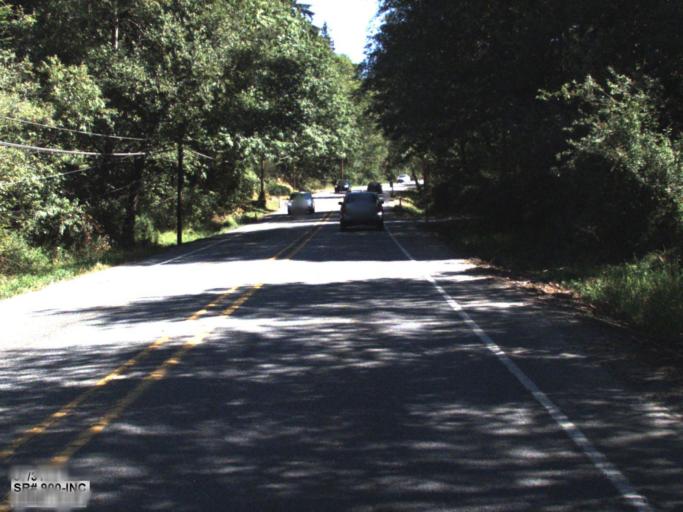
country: US
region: Washington
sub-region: King County
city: East Renton Highlands
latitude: 47.5142
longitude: -122.0767
